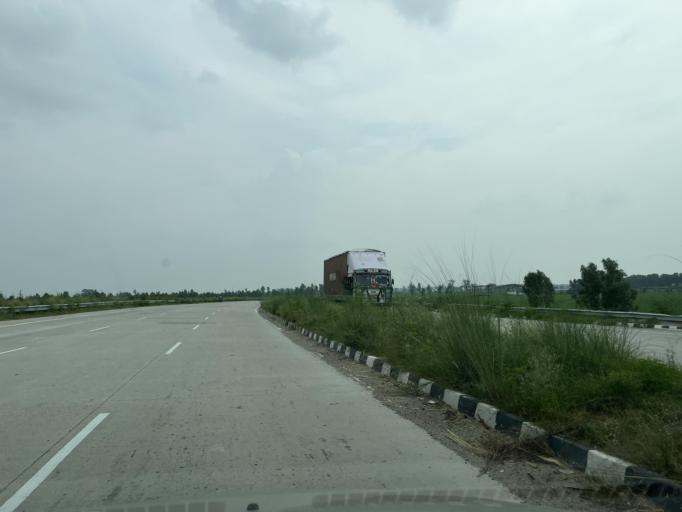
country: IN
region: Uttarakhand
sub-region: Udham Singh Nagar
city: Kashipur
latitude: 29.1891
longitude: 78.9393
